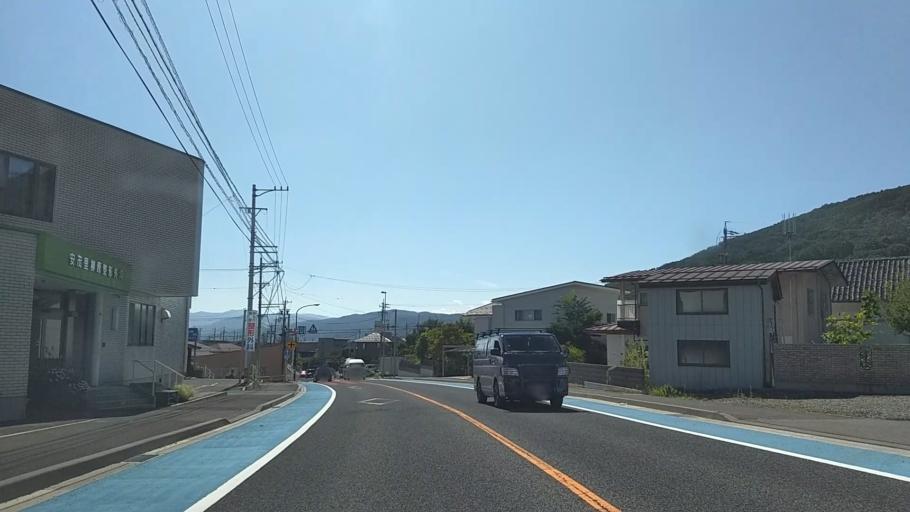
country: JP
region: Nagano
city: Nagano-shi
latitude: 36.6381
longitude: 138.1724
